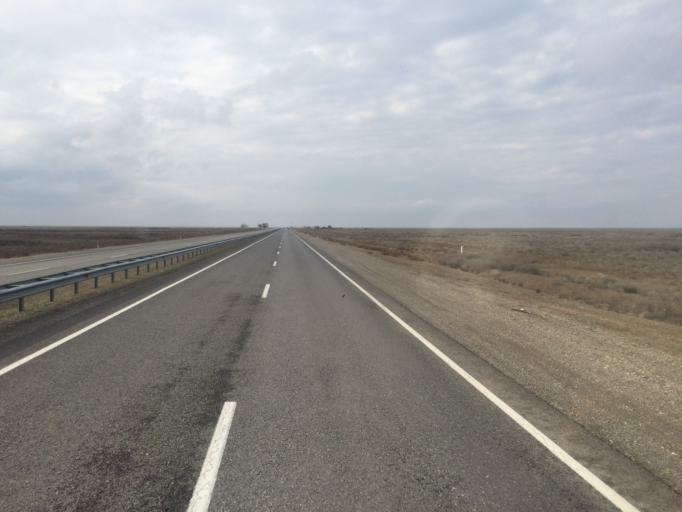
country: KZ
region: Ongtustik Qazaqstan
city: Turkestan
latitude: 43.5226
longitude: 67.8002
